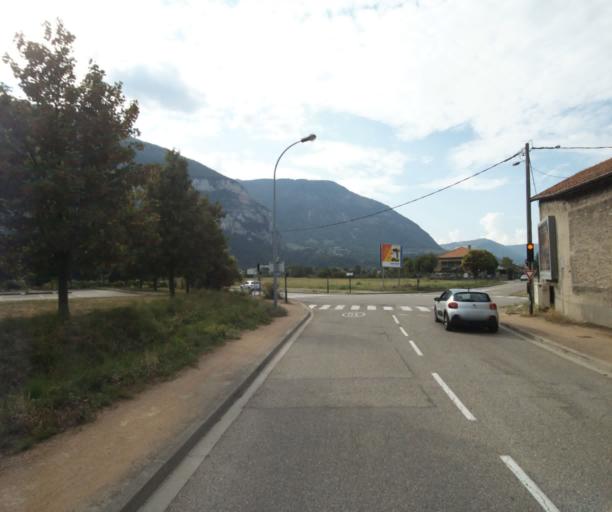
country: FR
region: Rhone-Alpes
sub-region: Departement de l'Isere
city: Fontaine
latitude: 45.2020
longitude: 5.6775
